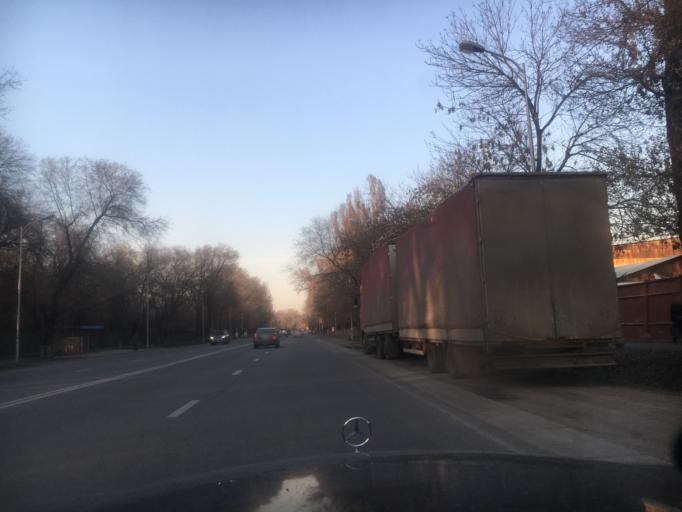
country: KZ
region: Almaty Oblysy
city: Pervomayskiy
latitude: 43.3479
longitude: 76.9698
